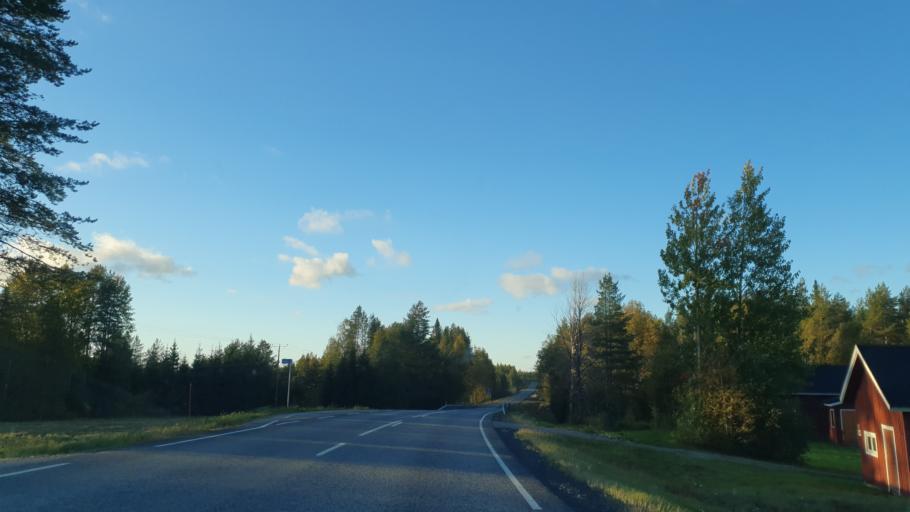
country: FI
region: Kainuu
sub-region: Kehys-Kainuu
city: Kuhmo
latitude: 64.0341
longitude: 29.5767
